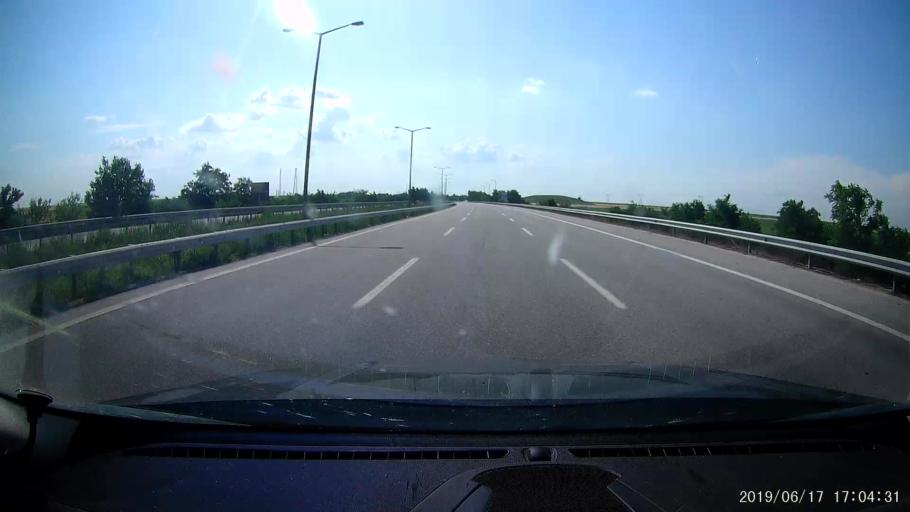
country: TR
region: Edirne
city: Haskoy
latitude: 41.6557
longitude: 26.7251
